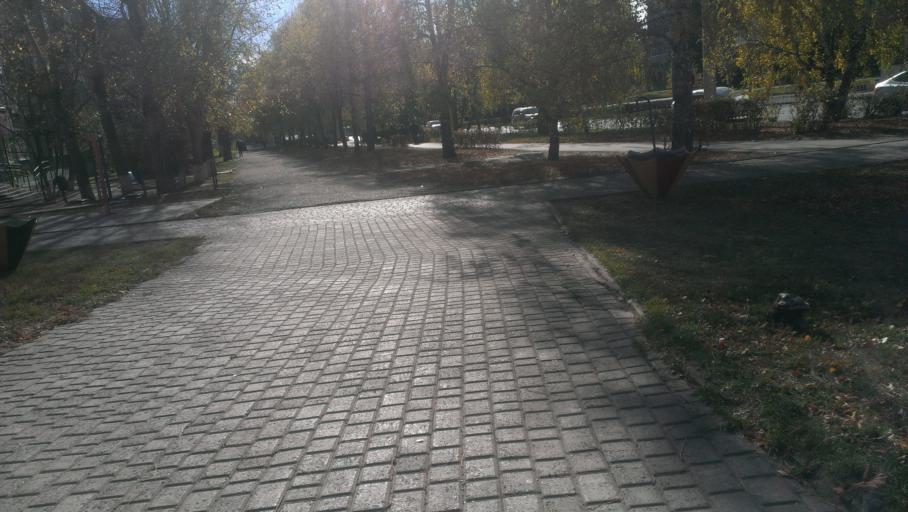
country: RU
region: Altai Krai
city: Novosilikatnyy
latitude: 53.3545
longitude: 83.6848
